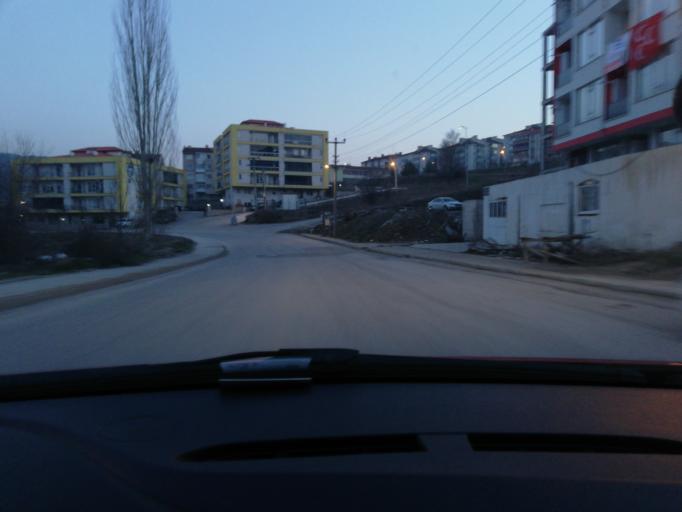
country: TR
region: Karabuk
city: Safranbolu
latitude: 41.2252
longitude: 32.6705
